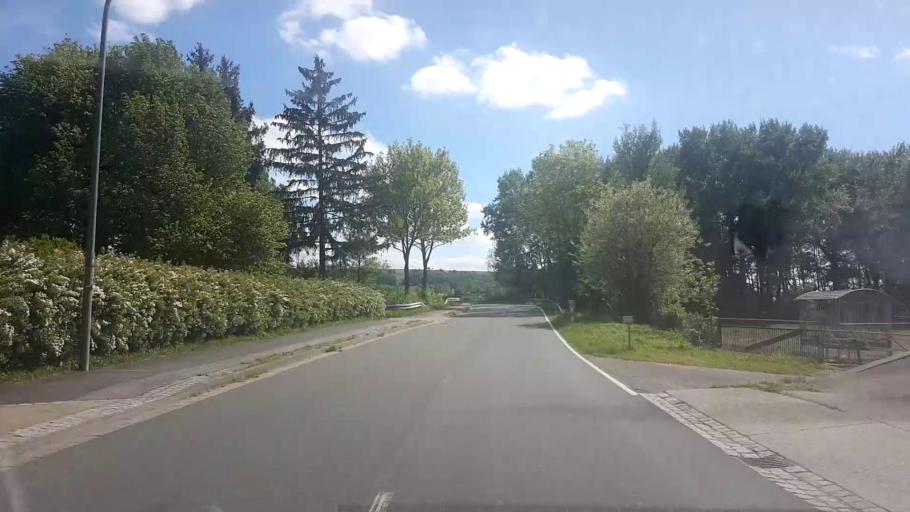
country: DE
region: Bavaria
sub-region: Regierungsbezirk Unterfranken
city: Untermerzbach
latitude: 50.1337
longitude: 10.8847
